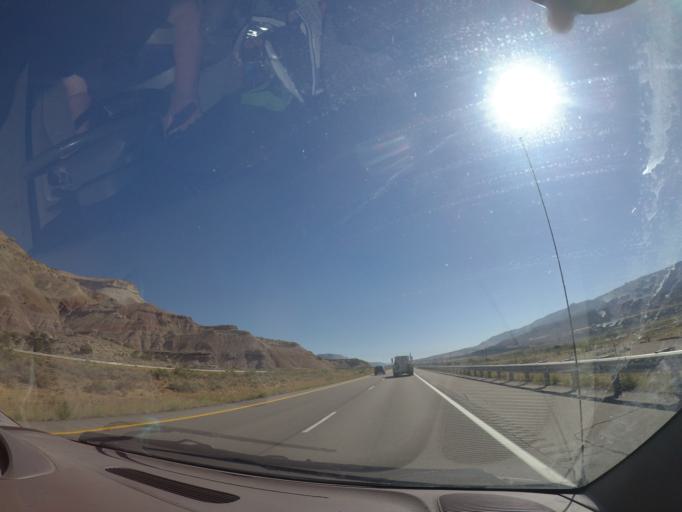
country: US
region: Colorado
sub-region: Garfield County
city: Parachute
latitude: 39.4044
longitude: -108.1074
